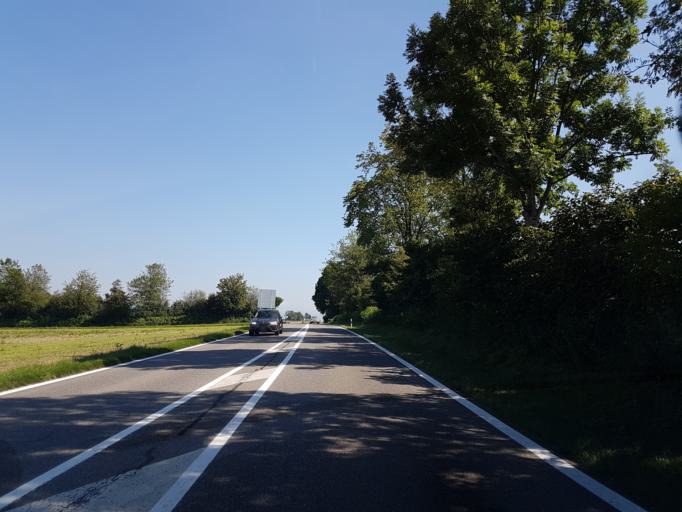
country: CH
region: Aargau
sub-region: Bezirk Muri
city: Waltenschwil
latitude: 47.3267
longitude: 8.2907
